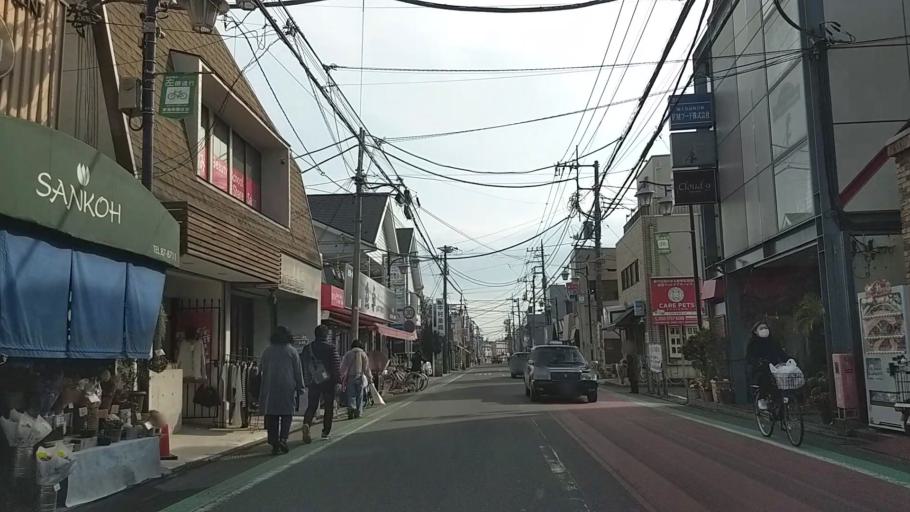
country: JP
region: Kanagawa
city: Chigasaki
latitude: 35.3284
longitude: 139.4076
